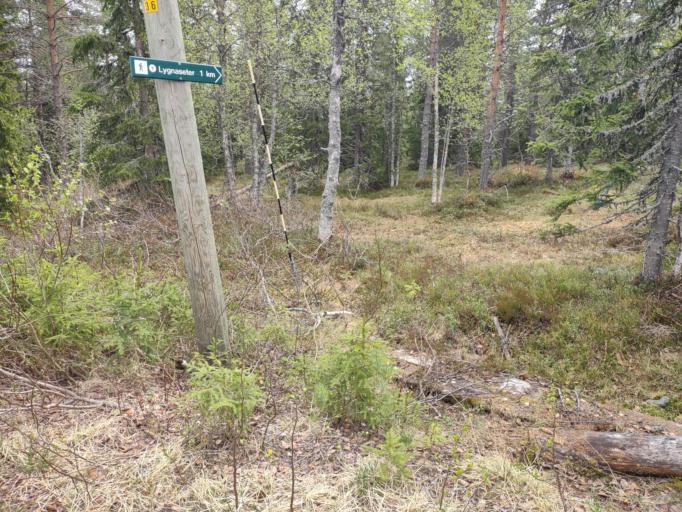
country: NO
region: Oppland
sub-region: Gran
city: Jaren
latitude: 60.4569
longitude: 10.6313
